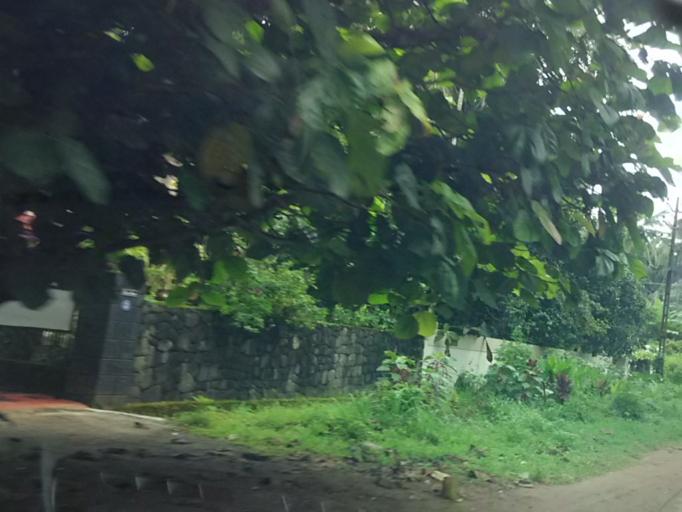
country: IN
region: Kerala
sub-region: Kozhikode
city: Kunnamangalam
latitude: 11.3137
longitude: 75.9240
